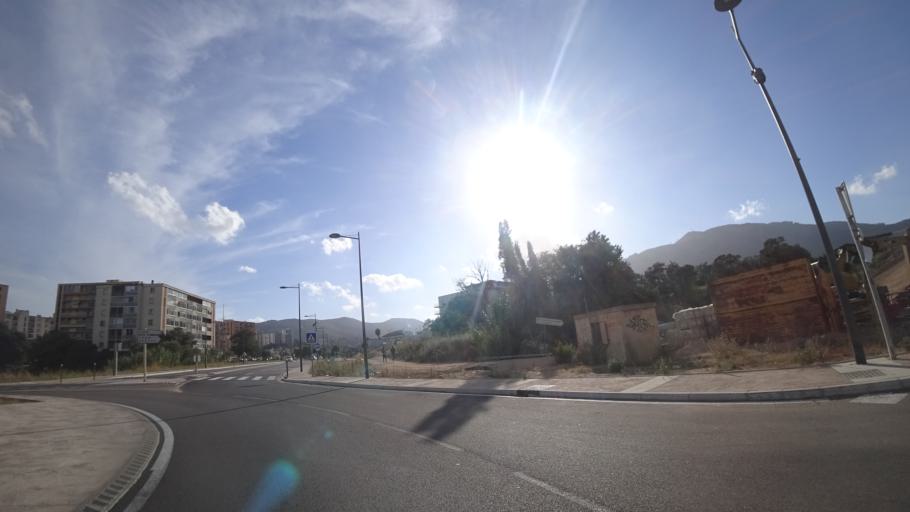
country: FR
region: Corsica
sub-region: Departement de la Corse-du-Sud
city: Ajaccio
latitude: 41.9389
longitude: 8.7418
